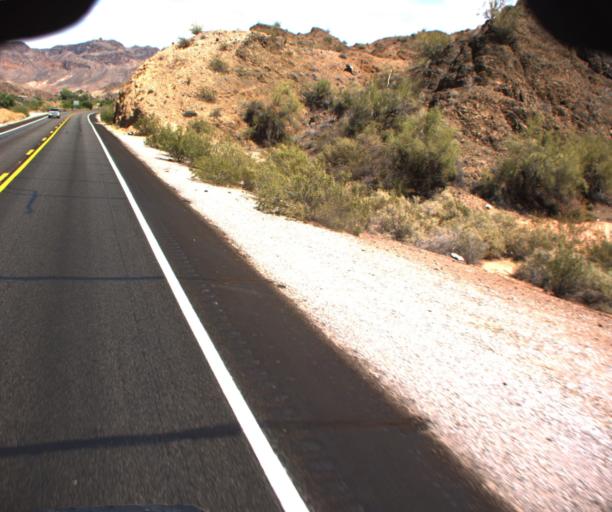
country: US
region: Arizona
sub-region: La Paz County
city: Cienega Springs
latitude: 34.2563
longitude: -114.1557
